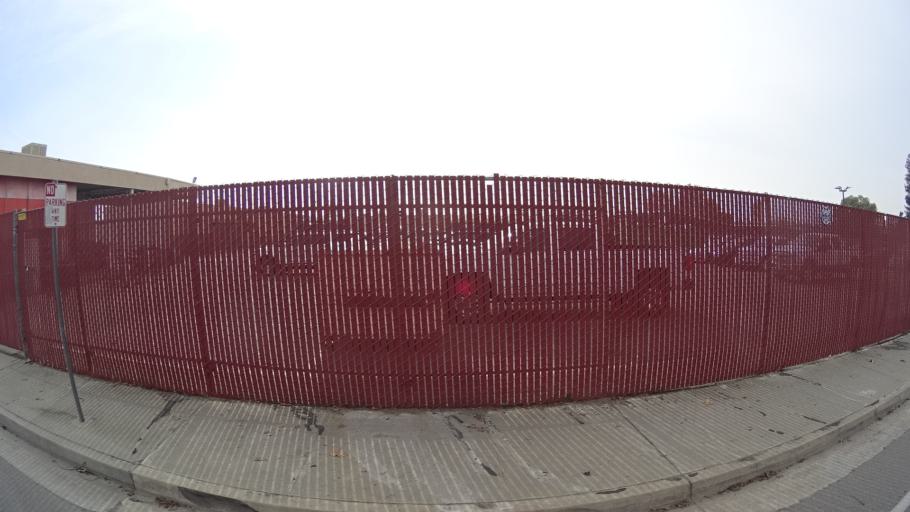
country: US
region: California
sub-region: Kern County
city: Bakersfield
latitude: 35.3780
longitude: -119.0413
